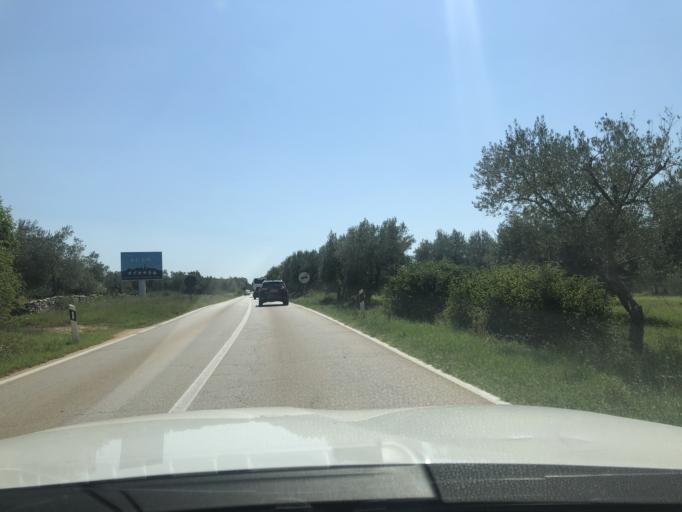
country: HR
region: Istarska
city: Vodnjan
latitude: 45.0253
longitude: 13.7996
